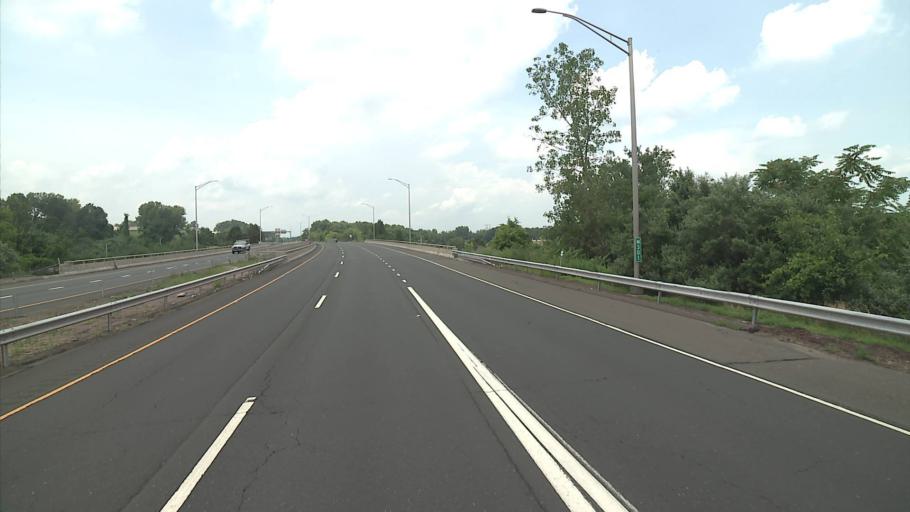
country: US
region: Connecticut
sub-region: Hartford County
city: East Hartford
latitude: 41.7924
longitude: -72.5704
